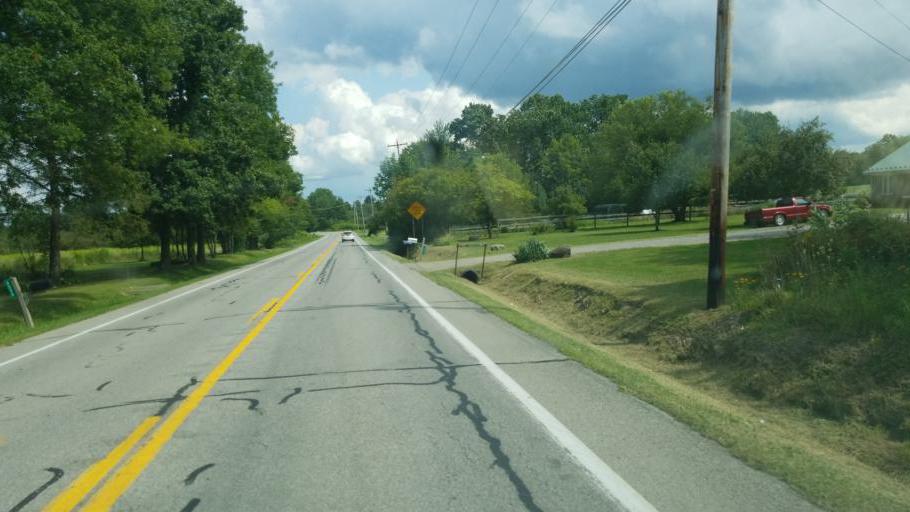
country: US
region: Pennsylvania
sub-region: Crawford County
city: Pymatuning Central
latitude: 41.6021
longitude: -80.4367
